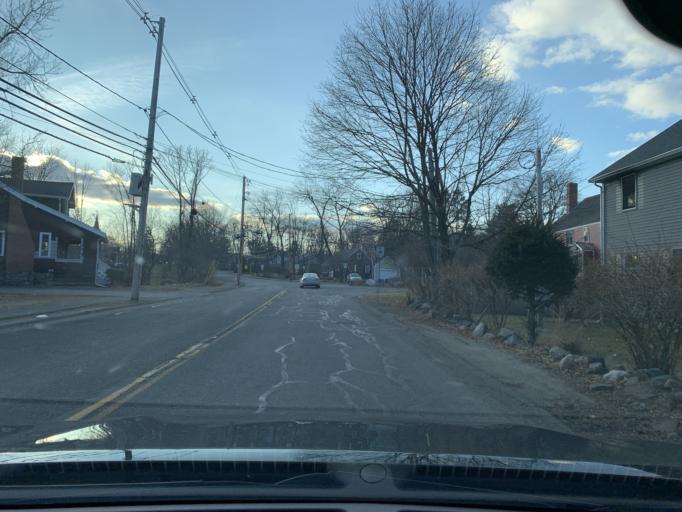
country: US
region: Massachusetts
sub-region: Essex County
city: Danvers
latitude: 42.5657
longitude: -70.9578
